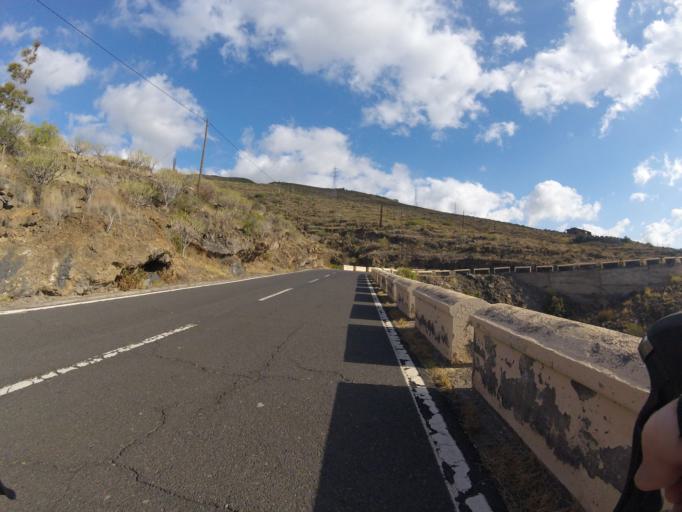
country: ES
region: Canary Islands
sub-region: Provincia de Santa Cruz de Tenerife
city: Candelaria
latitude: 28.3879
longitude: -16.3548
